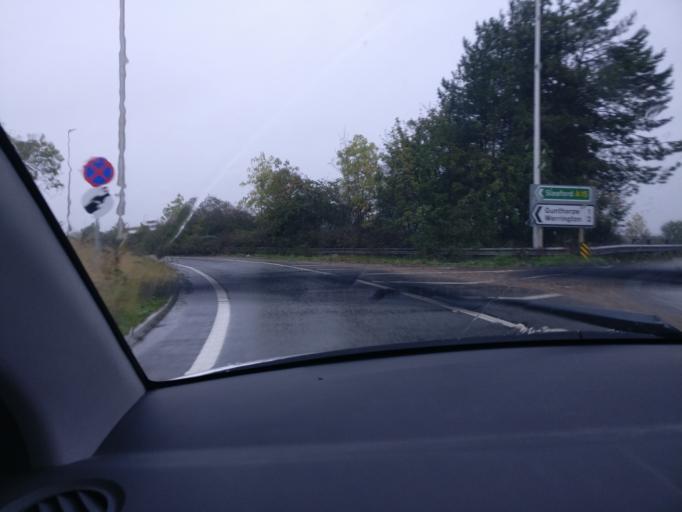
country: GB
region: England
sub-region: Peterborough
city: Newborough
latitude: 52.6050
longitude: -0.2304
